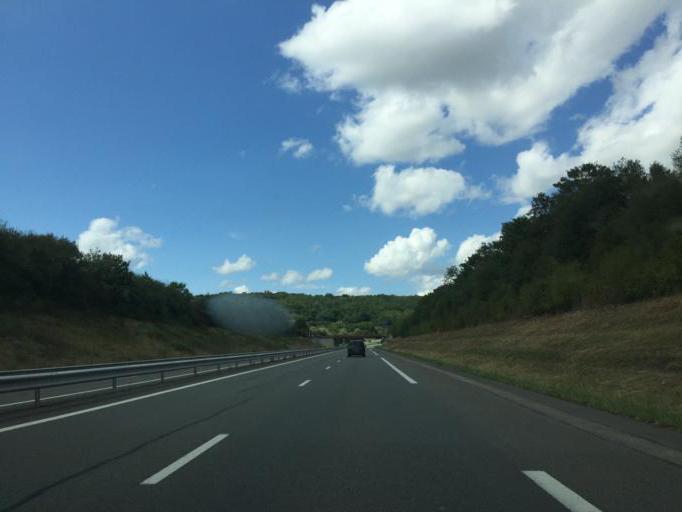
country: FR
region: Bourgogne
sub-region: Departement de Saone-et-Loire
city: Sance
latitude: 46.3459
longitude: 4.8330
